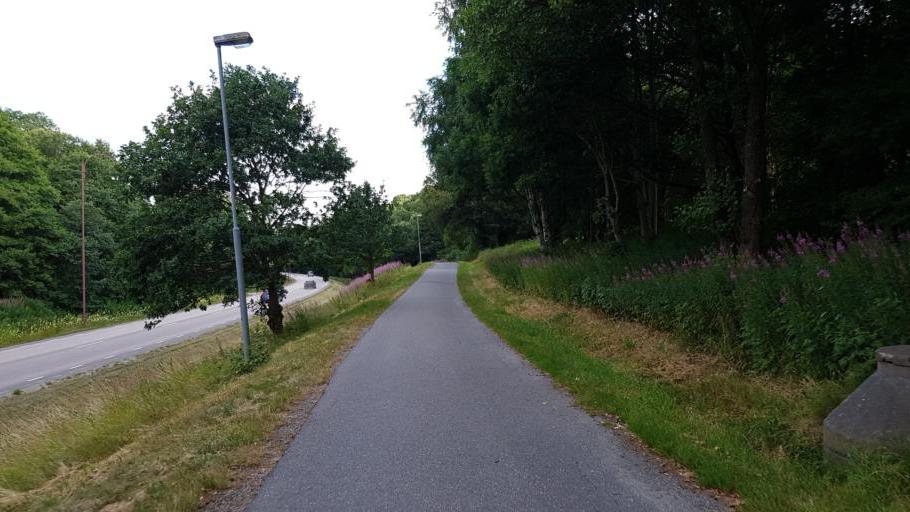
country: SE
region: Vaestra Goetaland
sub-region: Harryda Kommun
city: Molnlycke
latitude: 57.6584
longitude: 12.1047
